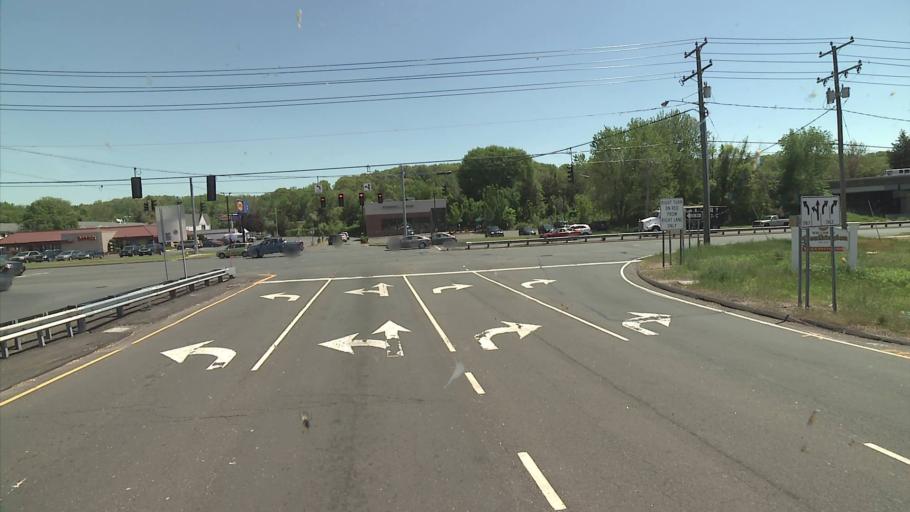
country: US
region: Connecticut
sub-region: Hartford County
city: Plainville
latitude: 41.6333
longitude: -72.8741
